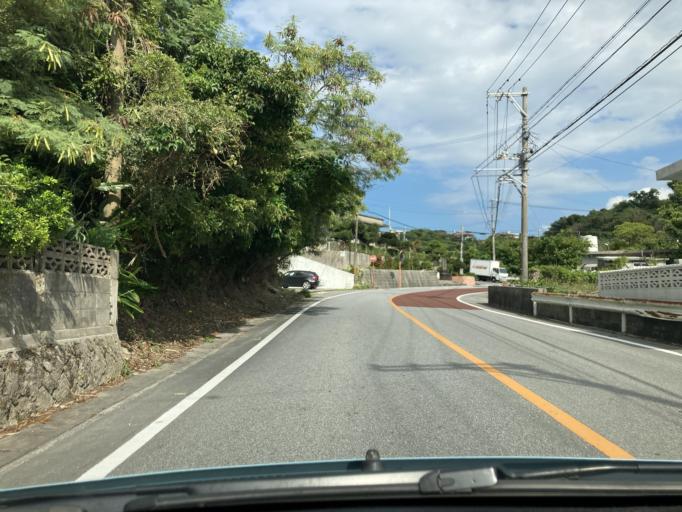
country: JP
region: Okinawa
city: Ginowan
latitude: 26.2694
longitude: 127.7838
